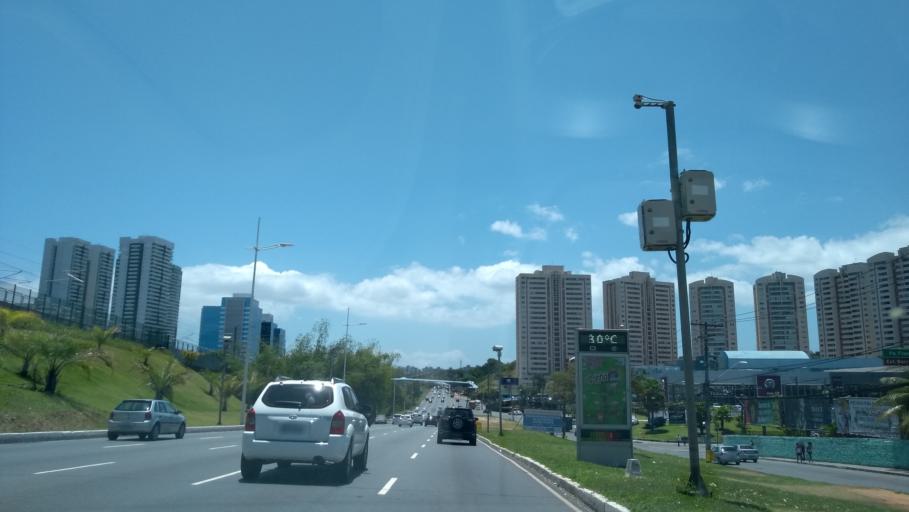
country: BR
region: Bahia
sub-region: Lauro De Freitas
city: Lauro de Freitas
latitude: -12.9379
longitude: -38.4084
